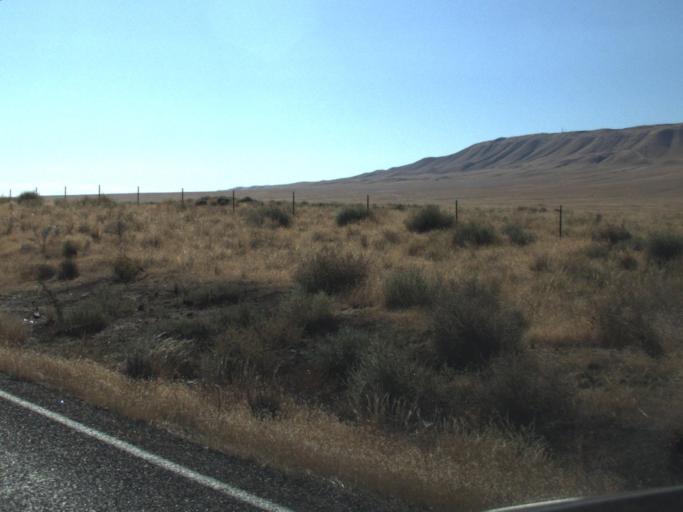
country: US
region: Washington
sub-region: Benton County
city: Benton City
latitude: 46.5010
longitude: -119.6138
